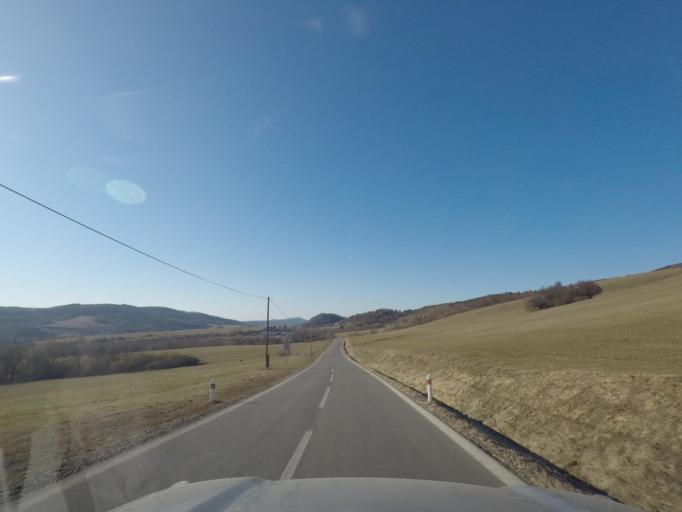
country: SK
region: Presovsky
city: Medzilaborce
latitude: 49.2163
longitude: 21.9834
